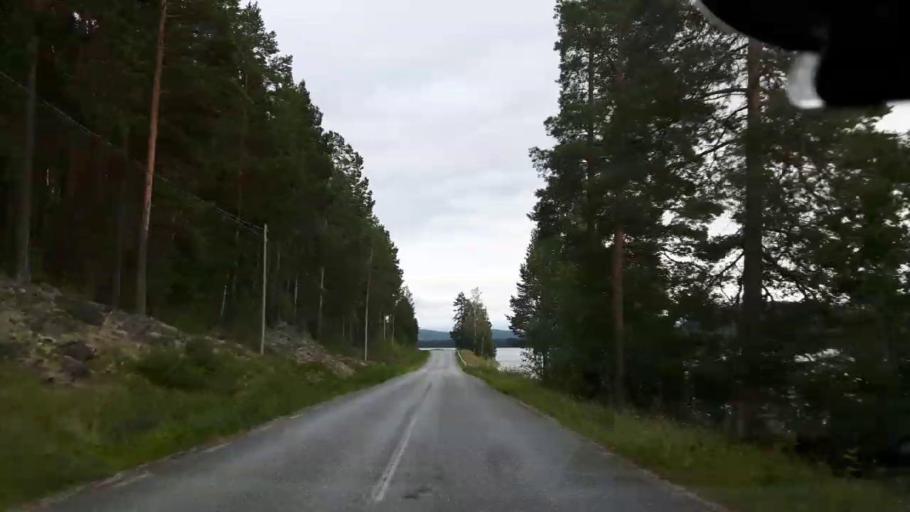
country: SE
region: Jaemtland
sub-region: Braecke Kommun
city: Braecke
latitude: 62.8664
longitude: 15.6172
